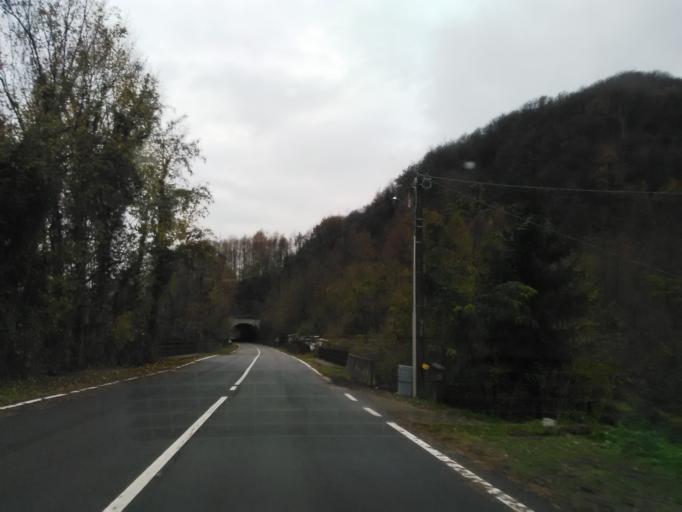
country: IT
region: Piedmont
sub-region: Provincia di Vercelli
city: Quarona
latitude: 45.7819
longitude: 8.2599
